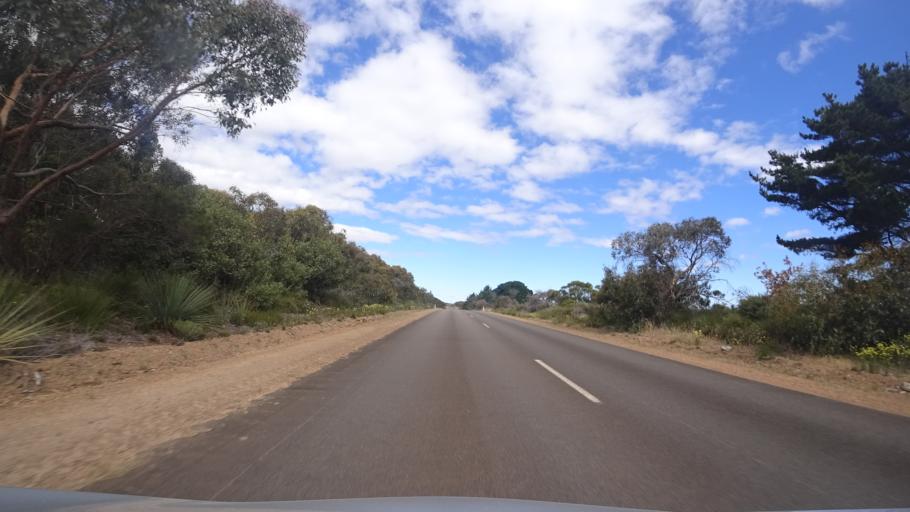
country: AU
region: South Australia
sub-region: Kangaroo Island
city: Kingscote
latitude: -35.7988
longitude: 137.0486
